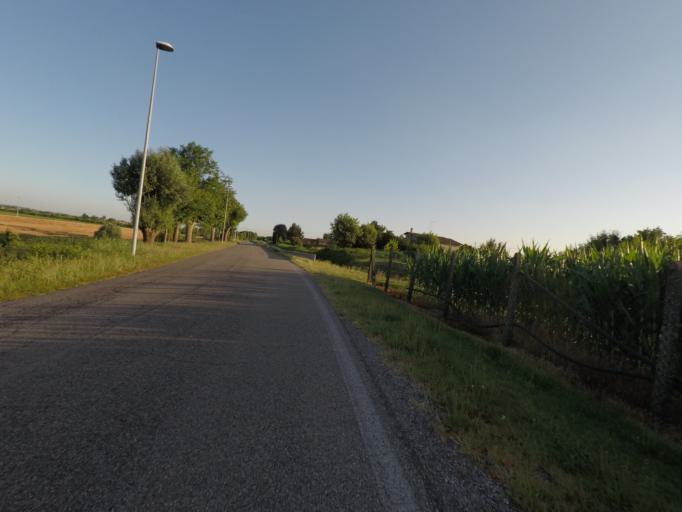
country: IT
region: Veneto
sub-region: Provincia di Rovigo
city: Fratta Polesine
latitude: 45.0429
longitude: 11.6470
